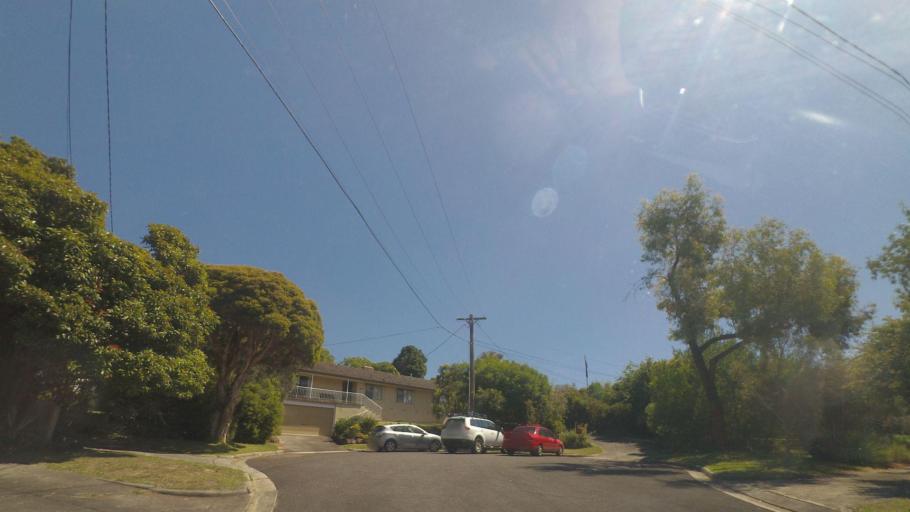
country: AU
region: Victoria
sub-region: Manningham
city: Park Orchards
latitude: -37.7955
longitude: 145.2306
